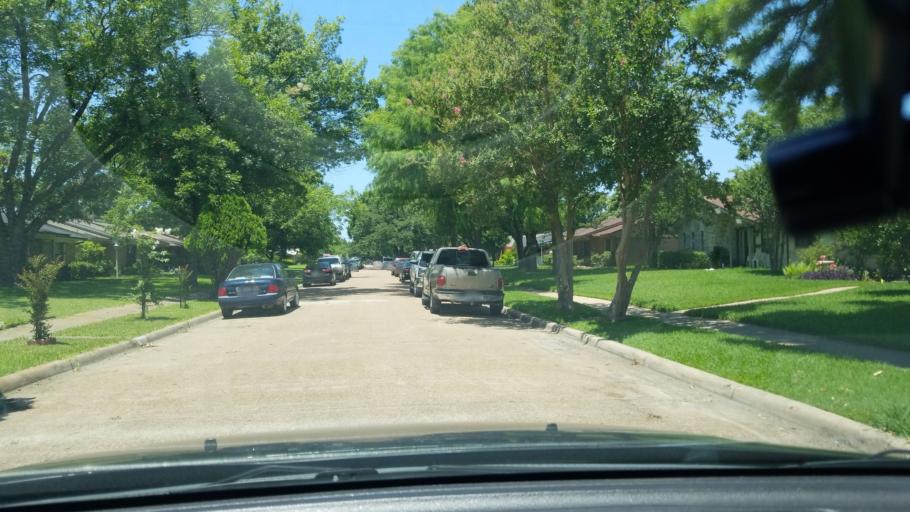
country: US
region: Texas
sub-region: Dallas County
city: Mesquite
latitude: 32.7962
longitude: -96.6473
